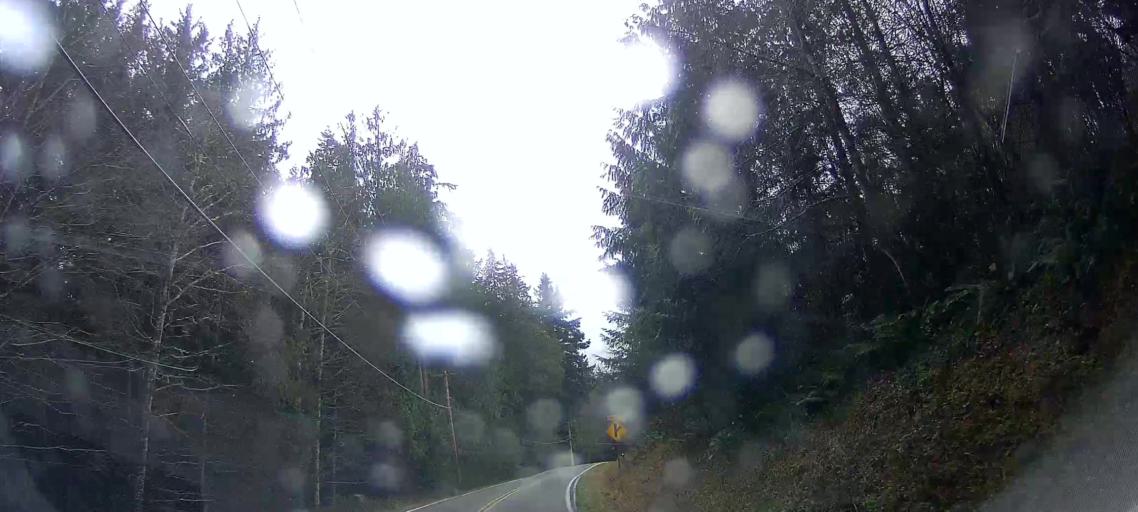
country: US
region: Washington
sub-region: Skagit County
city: Clear Lake
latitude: 48.4705
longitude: -122.1779
